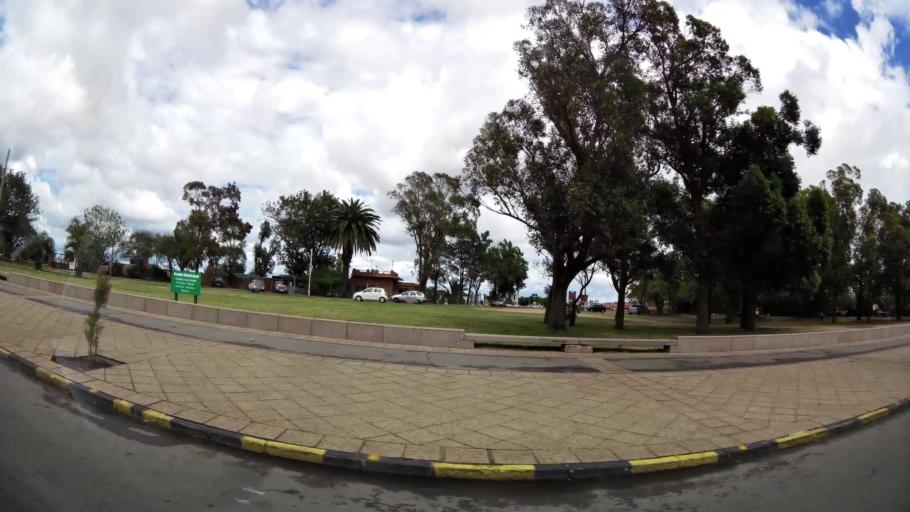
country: UY
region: Montevideo
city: Montevideo
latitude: -34.9200
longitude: -56.1711
